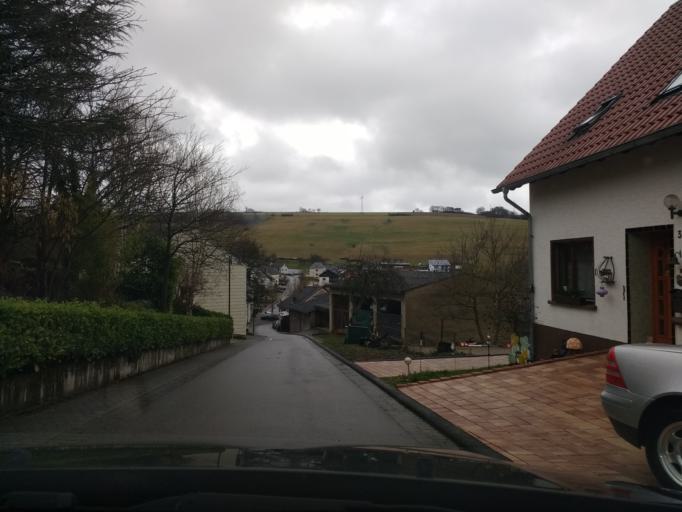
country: DE
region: Rheinland-Pfalz
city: Franzenheim
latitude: 49.6849
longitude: 6.6859
